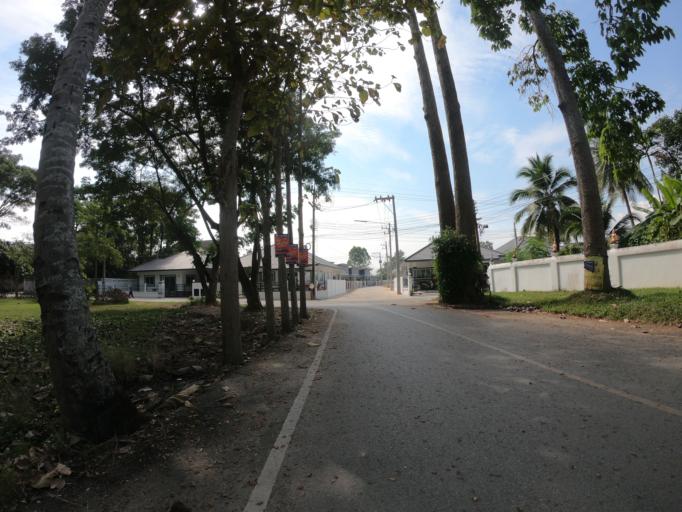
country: TH
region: Chiang Mai
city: San Sai
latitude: 18.8590
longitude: 99.0616
